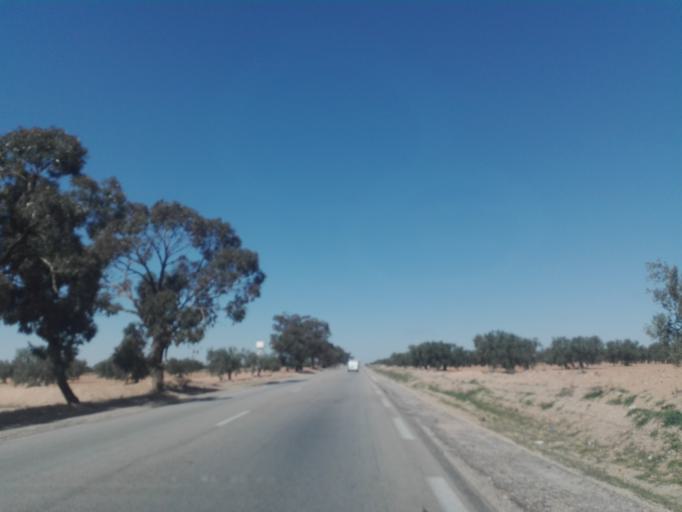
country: TN
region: Safaqis
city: Bi'r `Ali Bin Khalifah
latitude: 34.7583
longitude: 10.3096
